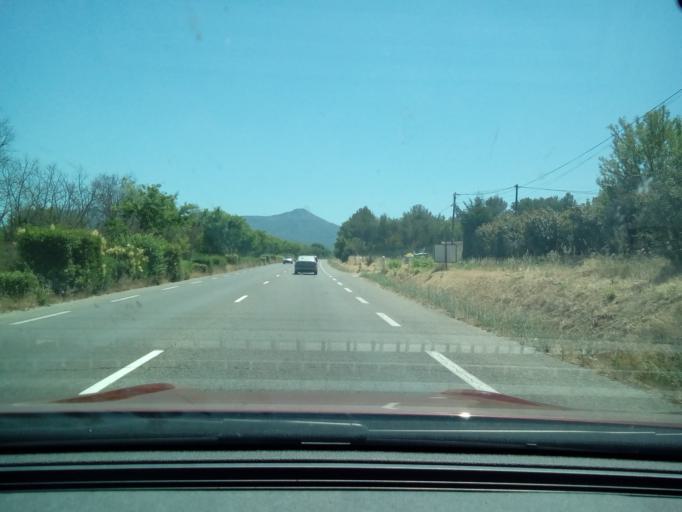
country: FR
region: Provence-Alpes-Cote d'Azur
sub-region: Departement des Bouches-du-Rhone
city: Trets
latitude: 43.4556
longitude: 5.6630
